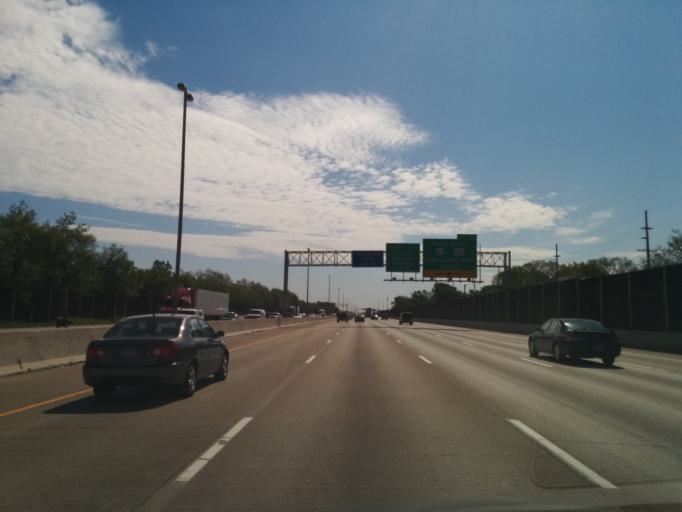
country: US
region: Indiana
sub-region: Lake County
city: Hammond
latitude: 41.5741
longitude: -87.4982
